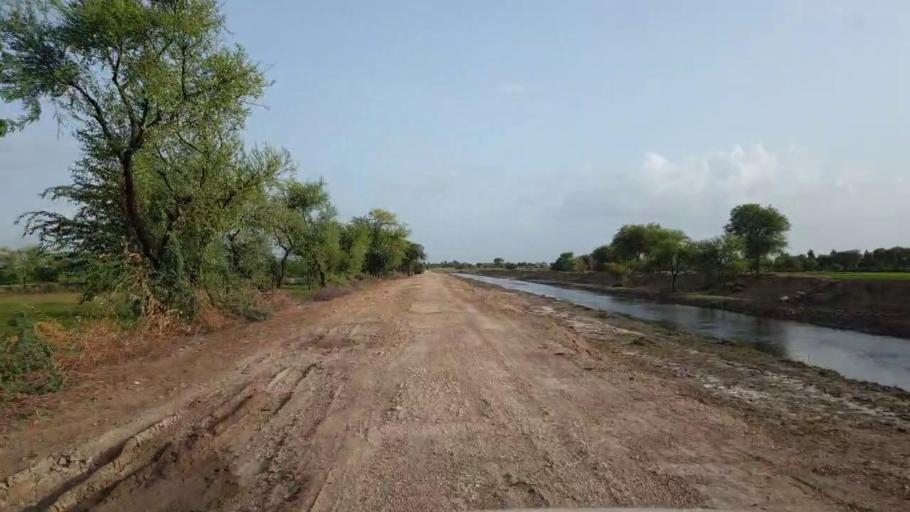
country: PK
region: Sindh
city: Kario
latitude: 24.8482
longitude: 68.6522
